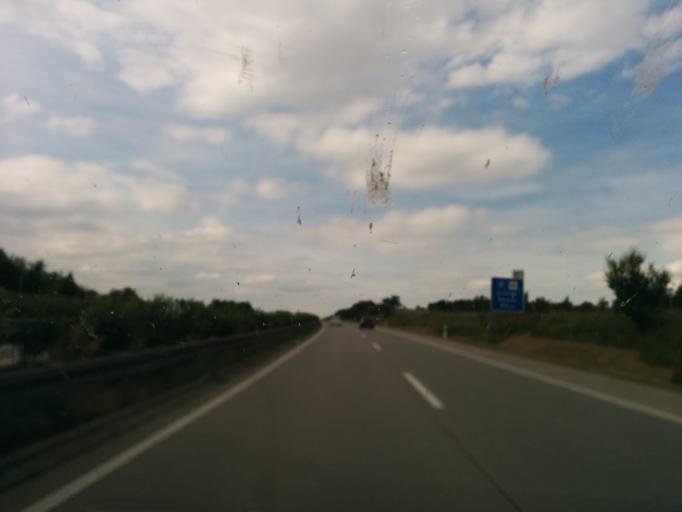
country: DE
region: Thuringia
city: Ingersleben
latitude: 50.9312
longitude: 10.9550
